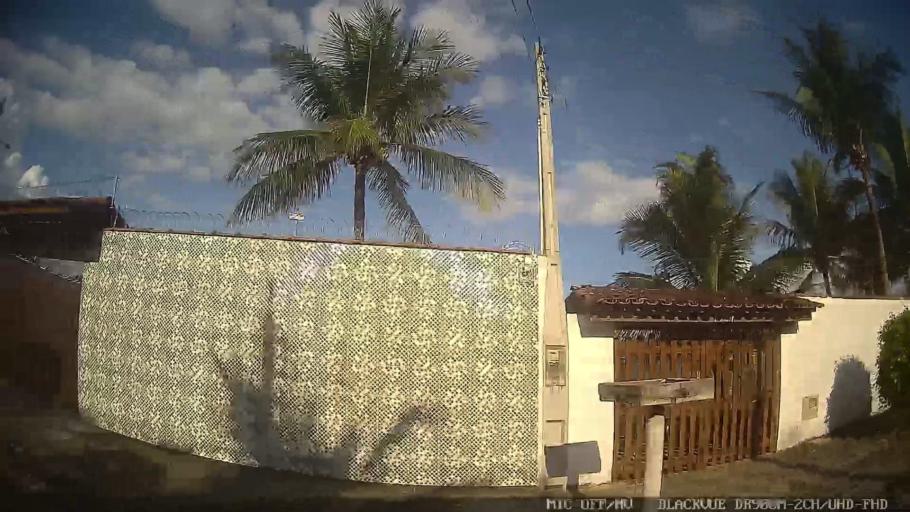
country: BR
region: Sao Paulo
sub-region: Caraguatatuba
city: Caraguatatuba
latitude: -23.6873
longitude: -45.4345
